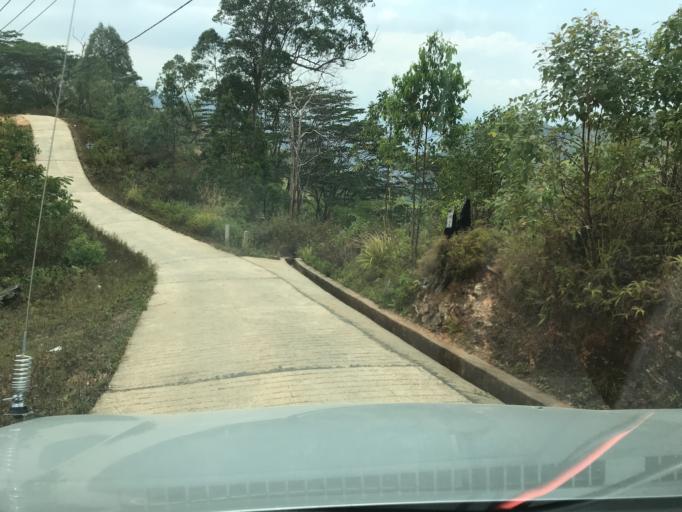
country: TL
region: Dili
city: Dili
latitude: -8.6140
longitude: 125.5710
